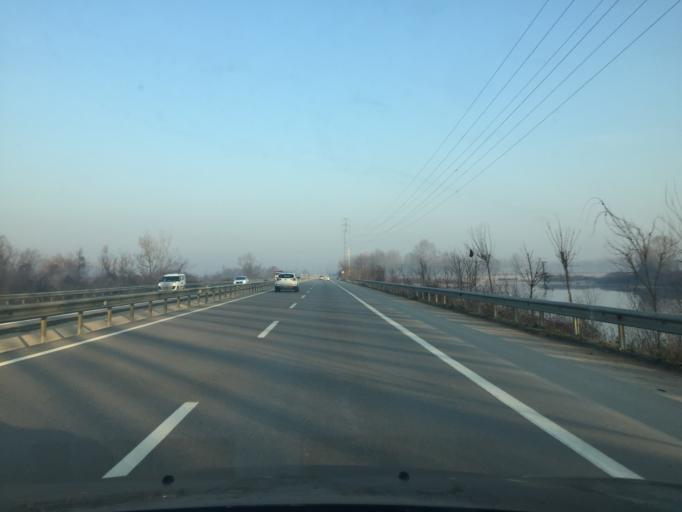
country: TR
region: Sakarya
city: Akyazi
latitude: 40.6832
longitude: 30.5767
